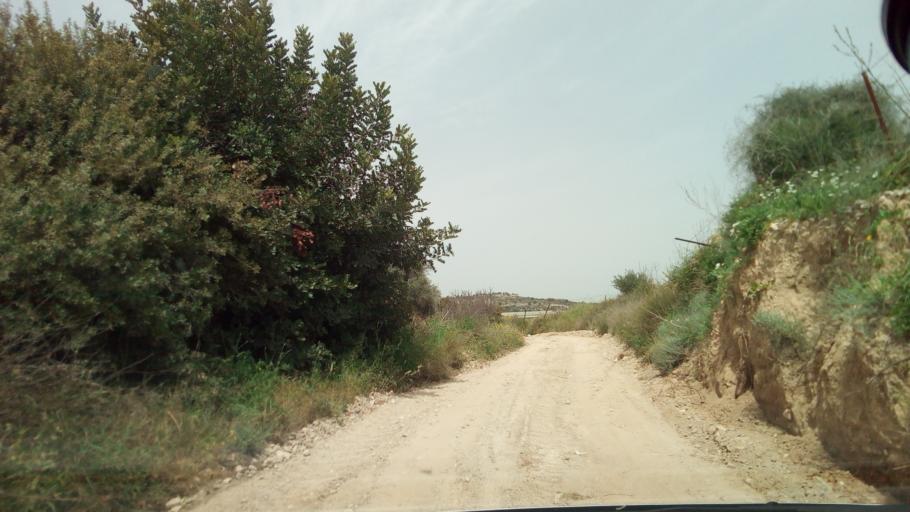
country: CY
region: Limassol
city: Pissouri
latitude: 34.6786
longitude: 32.7321
